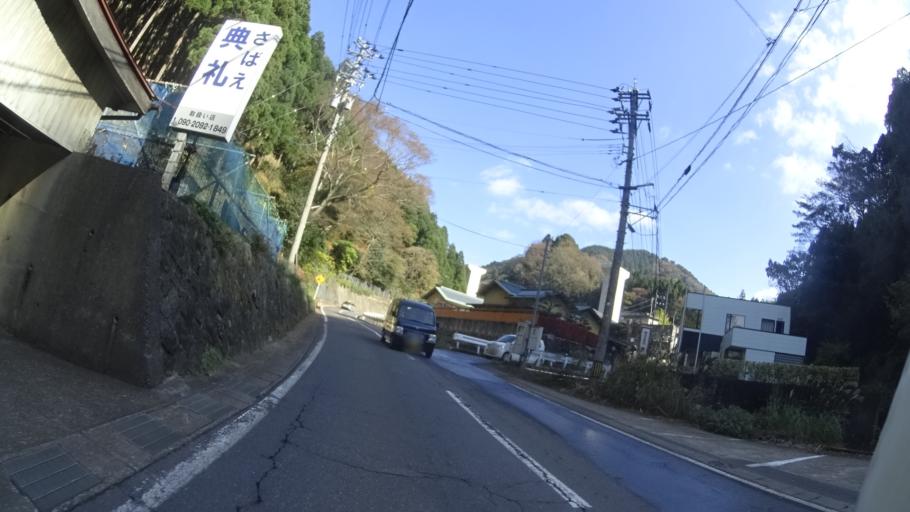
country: JP
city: Asahi
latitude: 35.9596
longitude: 135.9905
